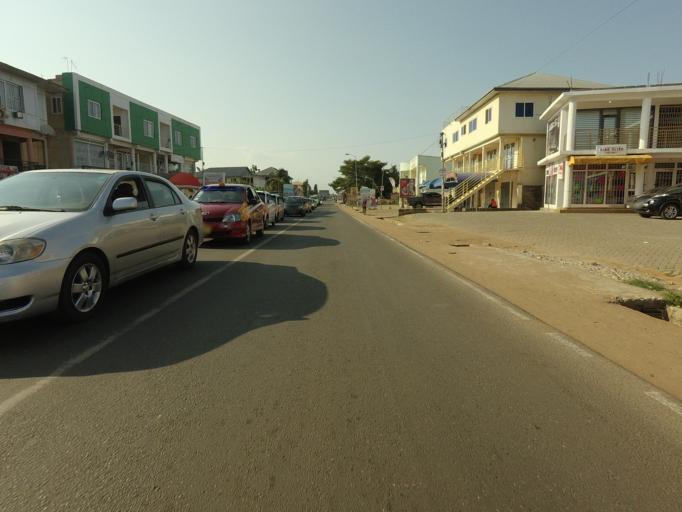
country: GH
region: Greater Accra
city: Nungua
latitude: 5.6270
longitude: -0.0762
